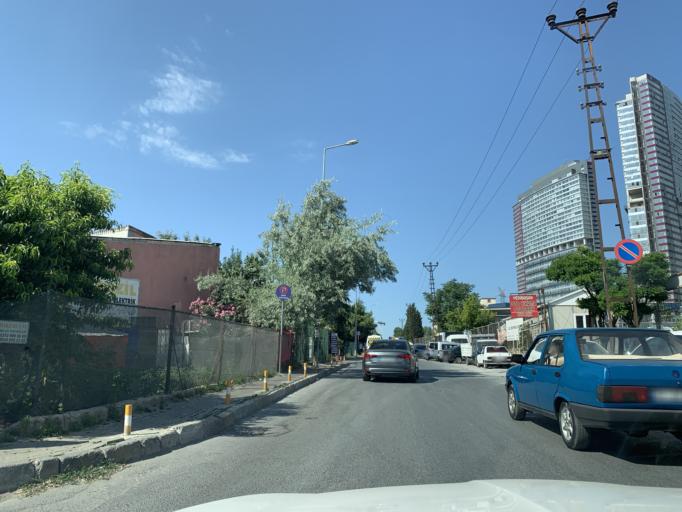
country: TR
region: Istanbul
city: Esenyurt
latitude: 41.0602
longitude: 28.6620
